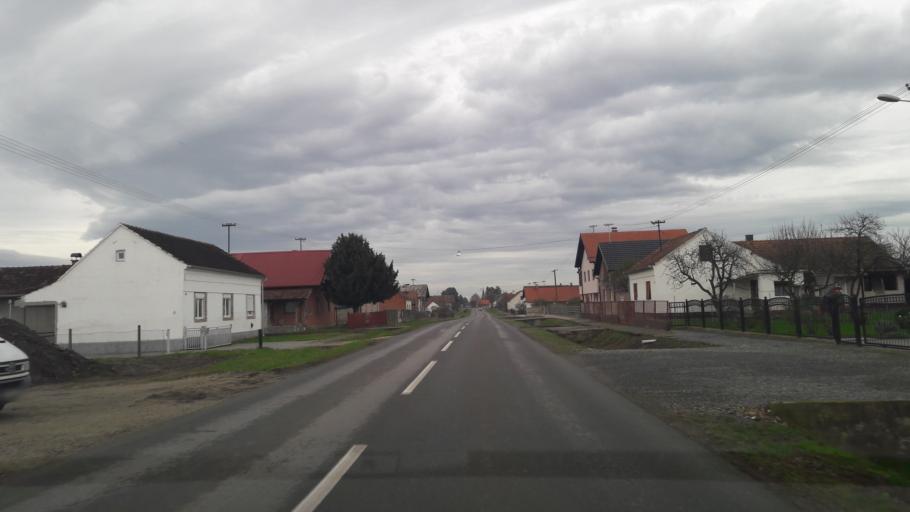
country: HR
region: Osjecko-Baranjska
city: Velimirovac
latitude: 45.5287
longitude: 18.0932
